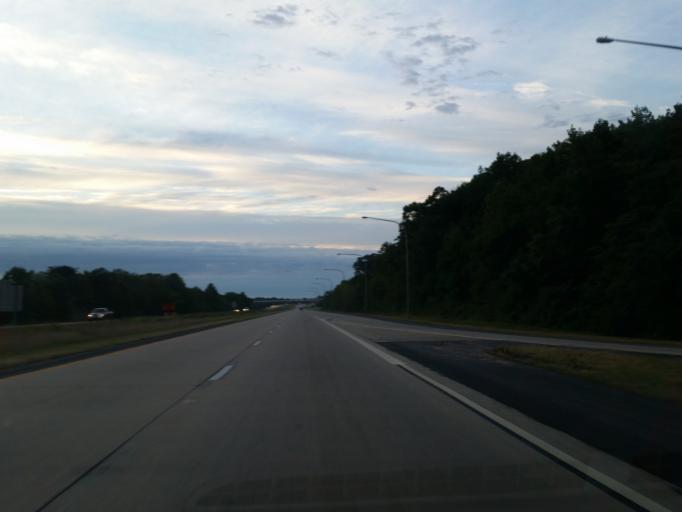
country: US
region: Delaware
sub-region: Kent County
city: Smyrna
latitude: 39.3259
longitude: -75.6170
